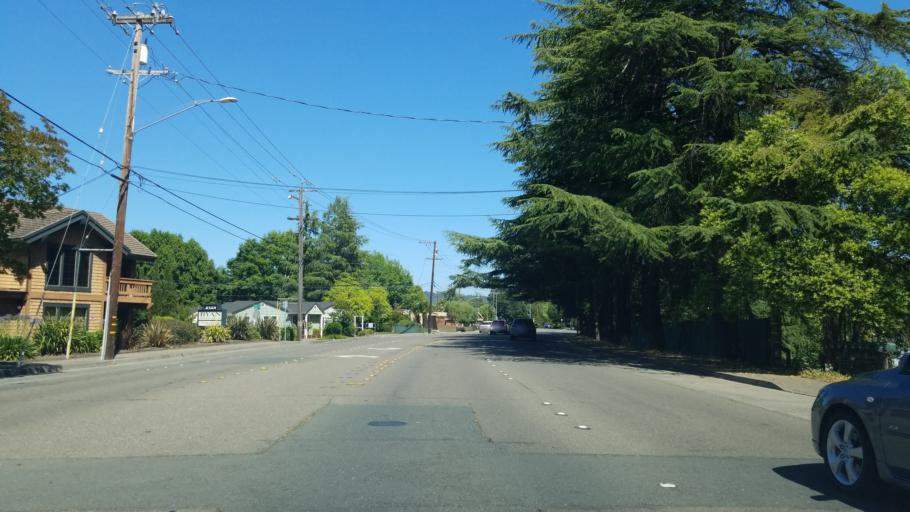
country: US
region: California
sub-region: Sonoma County
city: Santa Rosa
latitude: 38.4508
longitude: -122.6955
